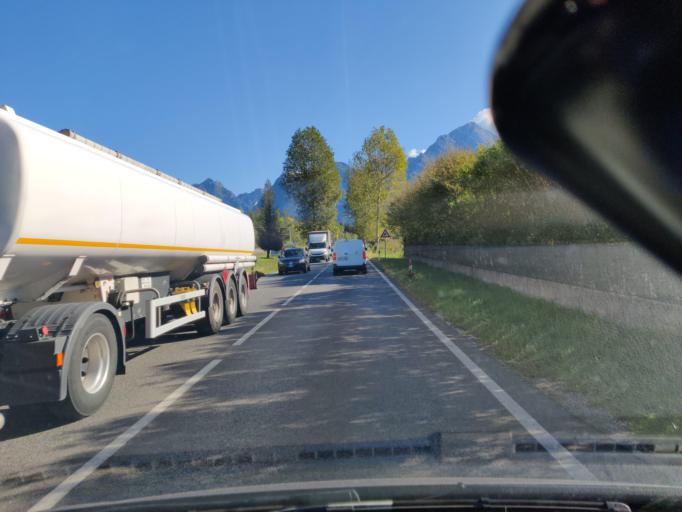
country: IT
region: Veneto
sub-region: Provincia di Belluno
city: Ponte nelle Alpi-Polpet
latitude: 46.1723
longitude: 12.2570
